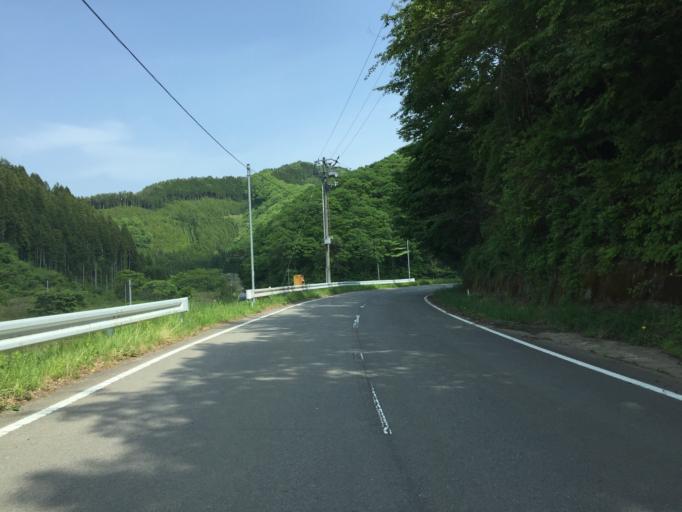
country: JP
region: Fukushima
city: Ishikawa
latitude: 36.9941
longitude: 140.6163
